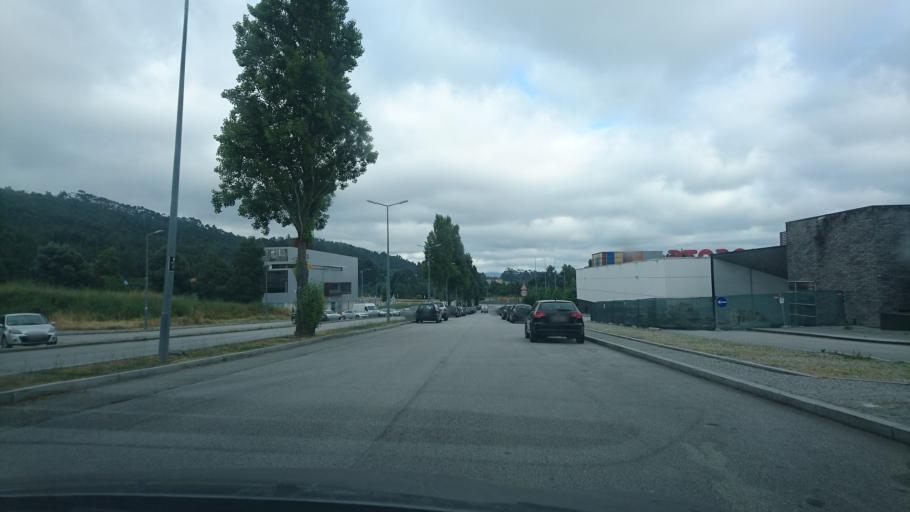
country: PT
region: Porto
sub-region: Valongo
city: Valongo
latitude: 41.1989
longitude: -8.4913
